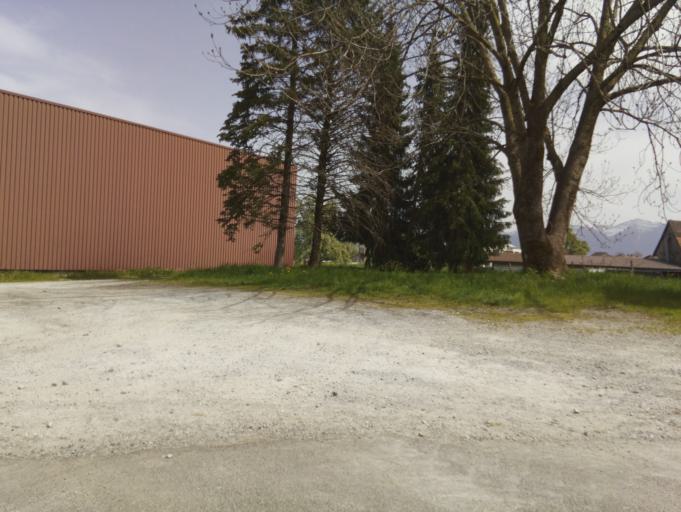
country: CH
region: Schwyz
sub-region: Bezirk March
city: Lachen
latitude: 47.1772
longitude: 8.8736
